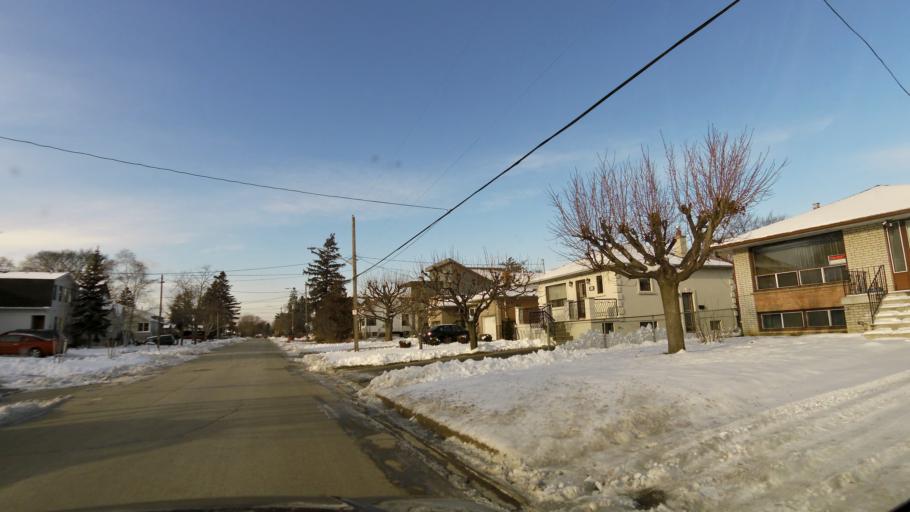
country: CA
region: Ontario
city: Etobicoke
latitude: 43.5811
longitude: -79.5697
